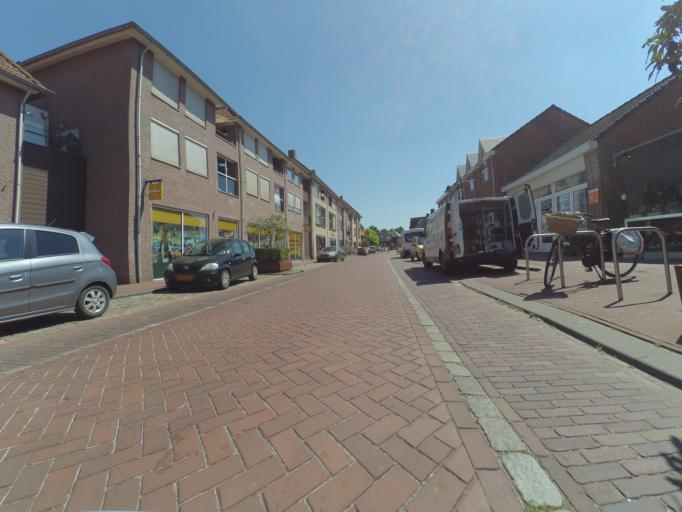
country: NL
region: North Brabant
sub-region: Gemeente Woensdrecht
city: Woensdrecht
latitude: 51.4252
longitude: 4.3229
